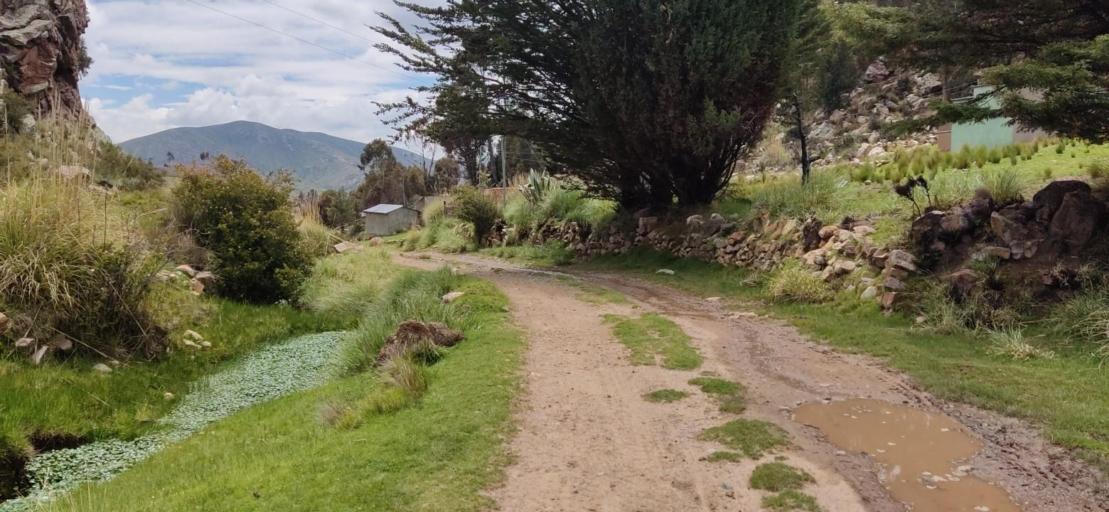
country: BO
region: La Paz
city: Batallas
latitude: -16.3468
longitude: -68.6428
